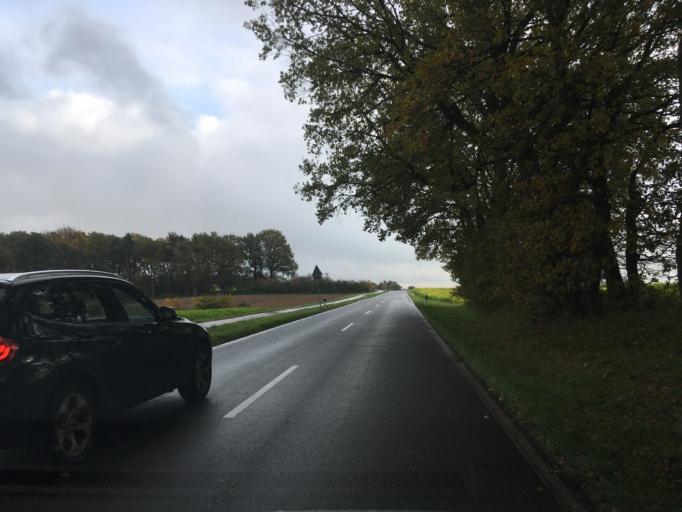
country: DE
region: North Rhine-Westphalia
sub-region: Regierungsbezirk Munster
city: Klein Reken
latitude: 51.8391
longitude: 7.0319
